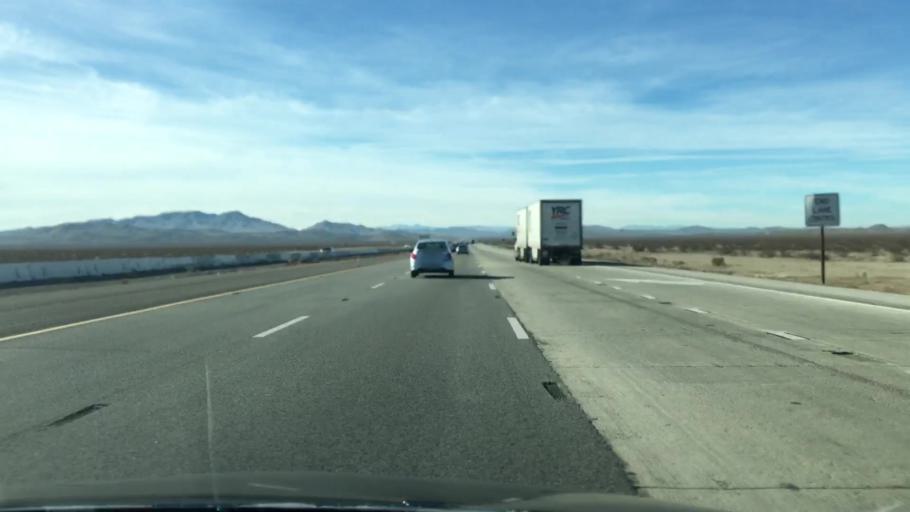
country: US
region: California
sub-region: San Bernardino County
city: Lenwood
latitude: 34.8040
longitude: -117.1038
